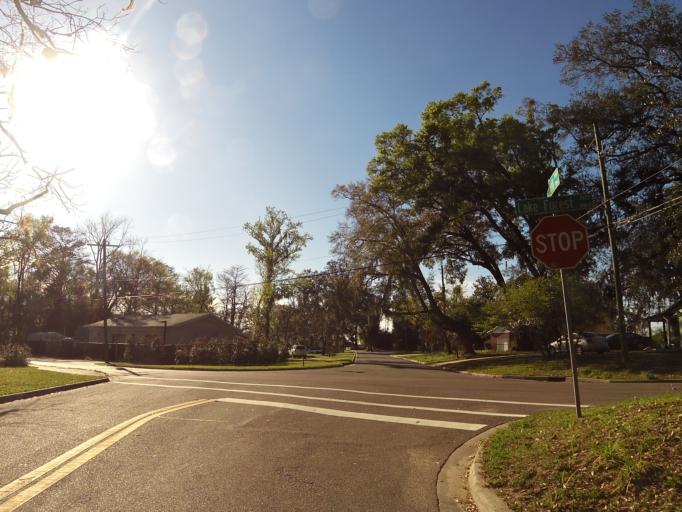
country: US
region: Florida
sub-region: Duval County
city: Jacksonville
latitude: 30.3950
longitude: -81.6774
